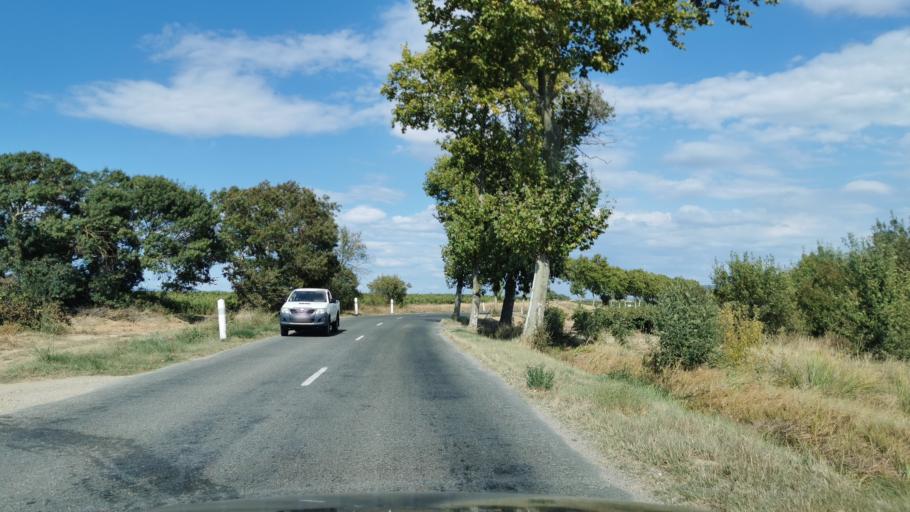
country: FR
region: Languedoc-Roussillon
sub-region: Departement de l'Aude
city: Azille
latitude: 43.2525
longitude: 2.6776
